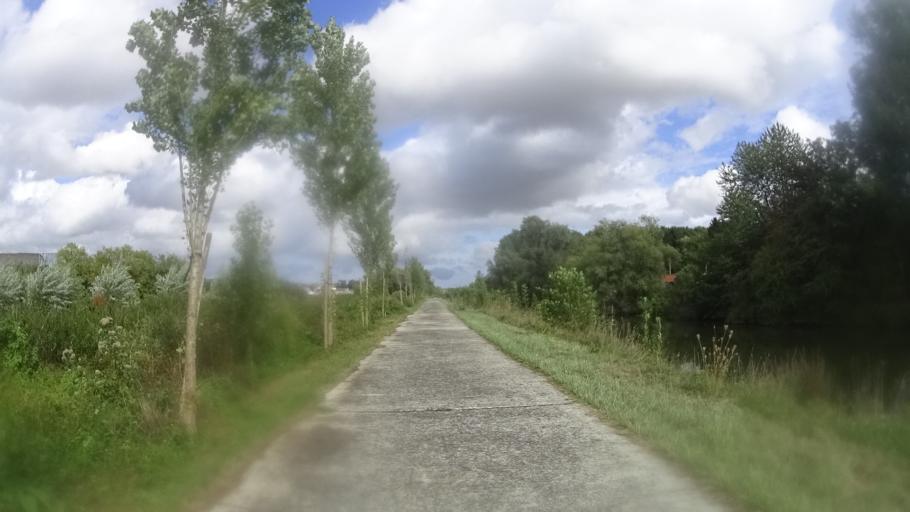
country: BE
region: Wallonia
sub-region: Province du Hainaut
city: Erquelinnes
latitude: 50.3075
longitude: 4.1259
